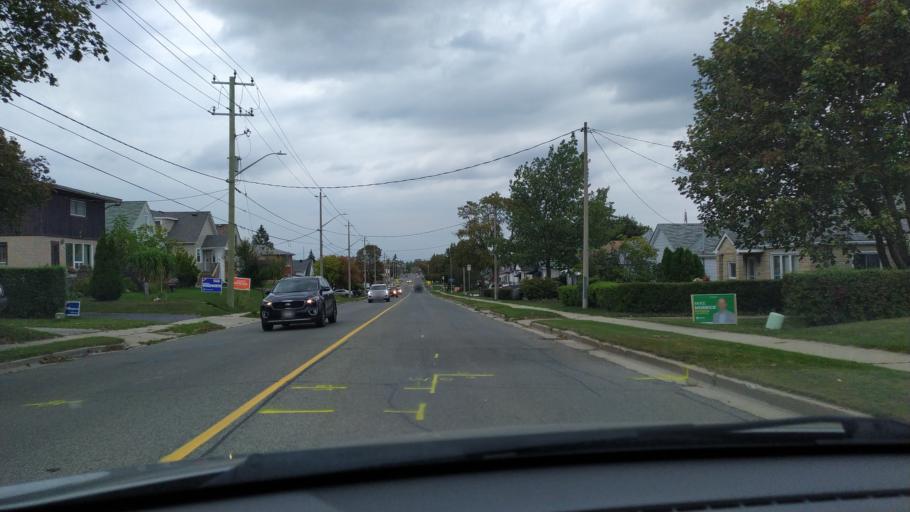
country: CA
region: Ontario
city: Waterloo
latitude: 43.4661
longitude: -80.4842
